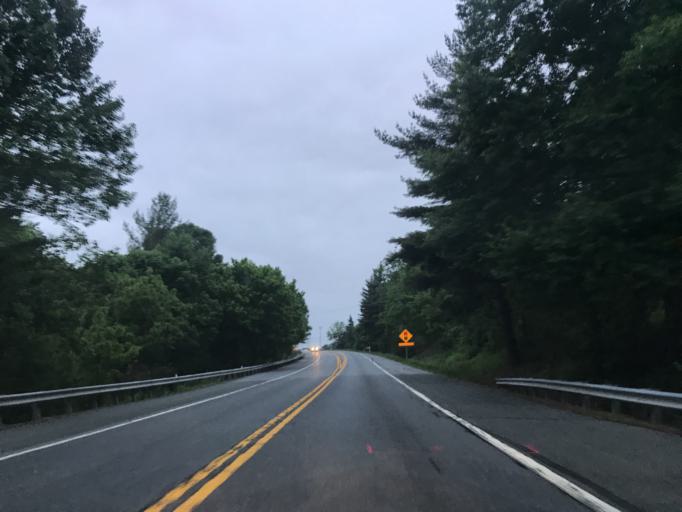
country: US
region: Maryland
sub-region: Frederick County
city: Linganore
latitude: 39.4390
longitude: -77.2523
